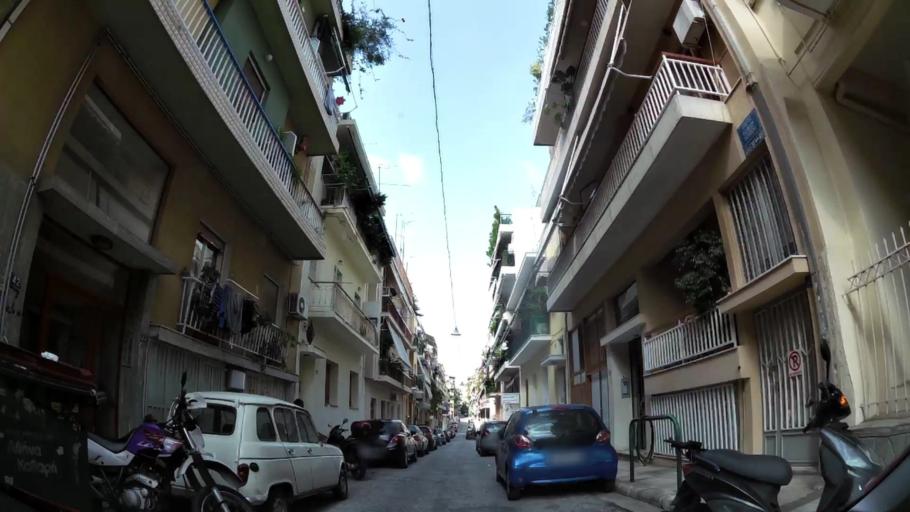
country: GR
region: Attica
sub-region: Nomarchia Athinas
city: Dhafni
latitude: 37.9593
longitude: 23.7306
